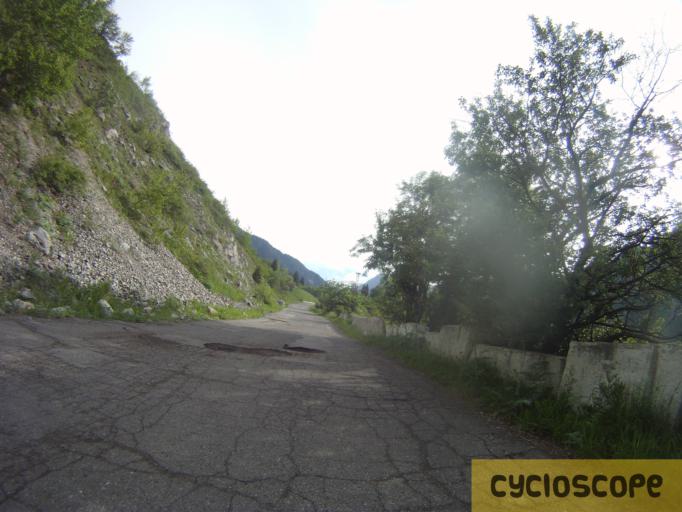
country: KZ
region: Almaty Oblysy
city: Esik
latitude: 43.2617
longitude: 77.4918
